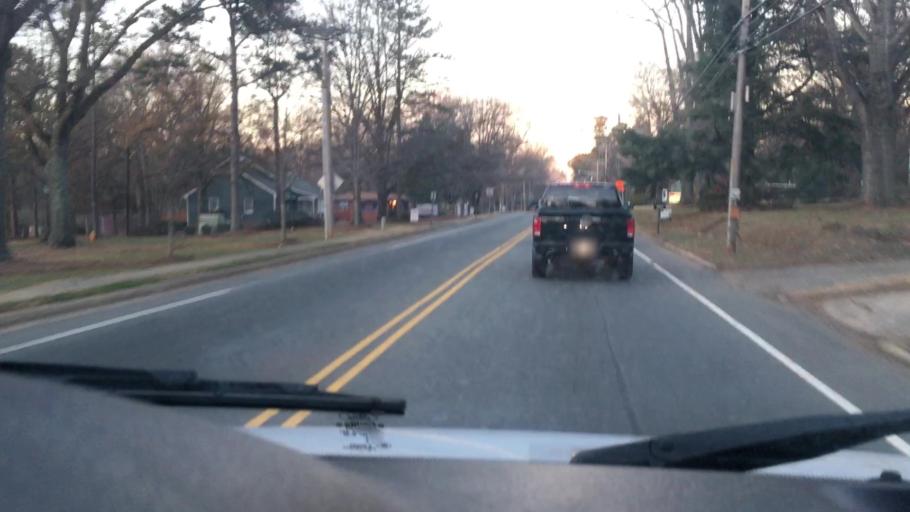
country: US
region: North Carolina
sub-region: Mecklenburg County
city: Huntersville
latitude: 35.4149
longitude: -80.8430
